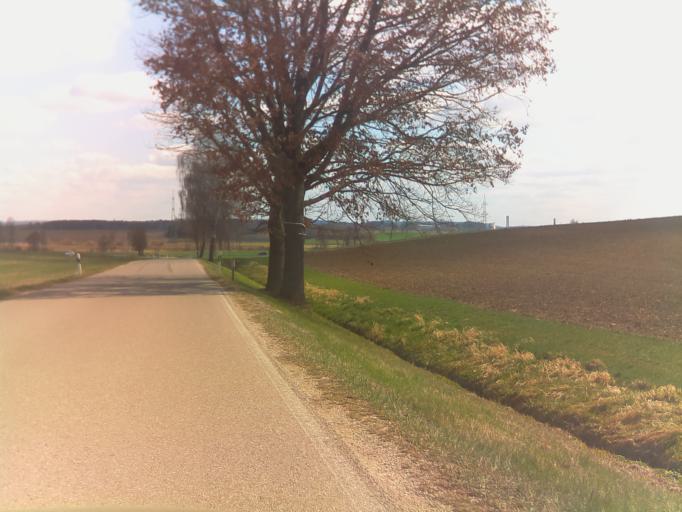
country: DE
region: Bavaria
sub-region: Swabia
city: Gablingen
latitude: 48.4681
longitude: 10.8124
